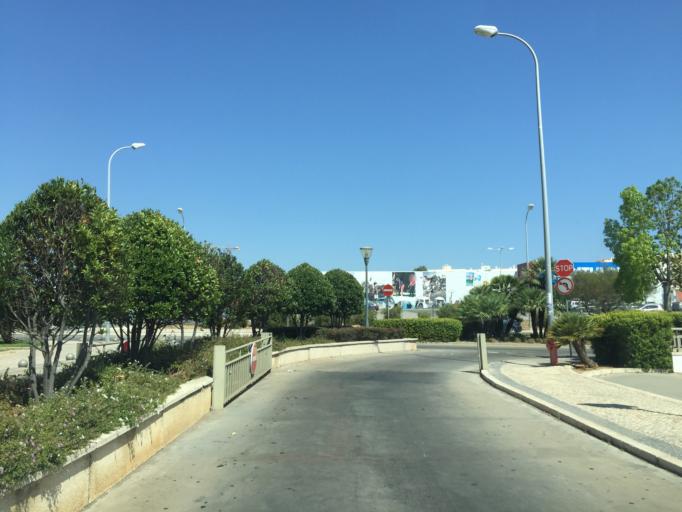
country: PT
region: Faro
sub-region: Faro
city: Faro
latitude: 37.0282
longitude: -7.9436
